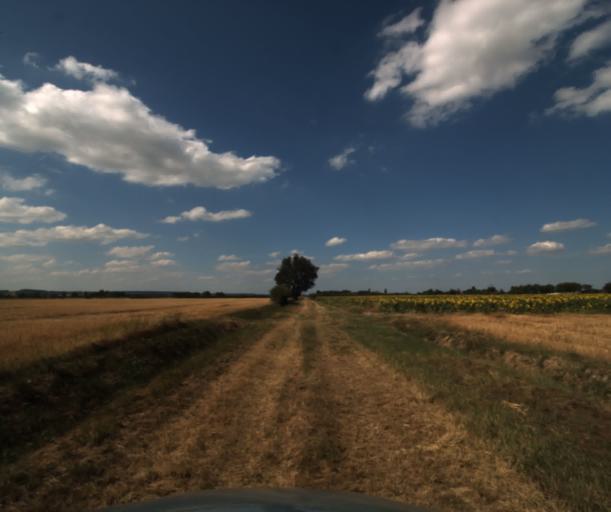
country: FR
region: Midi-Pyrenees
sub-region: Departement de la Haute-Garonne
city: Saint-Lys
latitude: 43.5229
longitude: 1.1777
